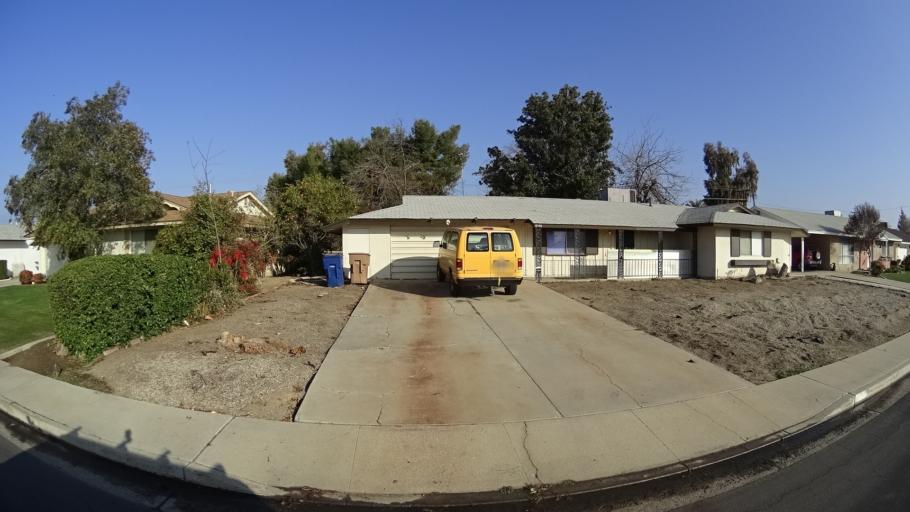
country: US
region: California
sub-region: Kern County
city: Greenacres
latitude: 35.3514
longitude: -119.0689
